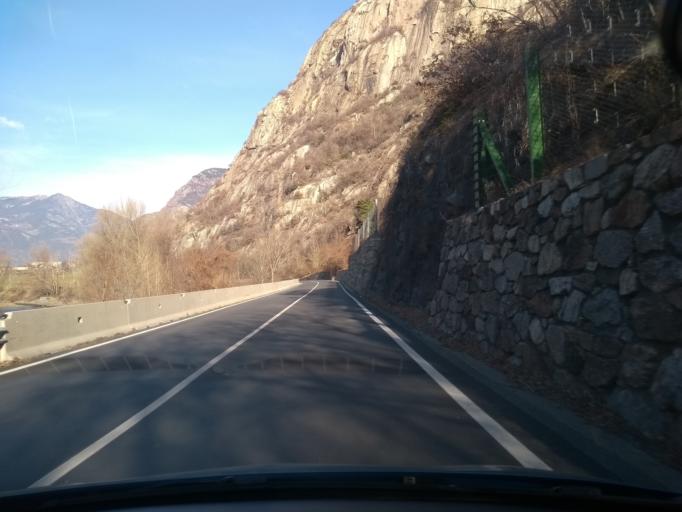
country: IT
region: Aosta Valley
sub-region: Valle d'Aosta
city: Hone
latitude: 45.6288
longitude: 7.7362
